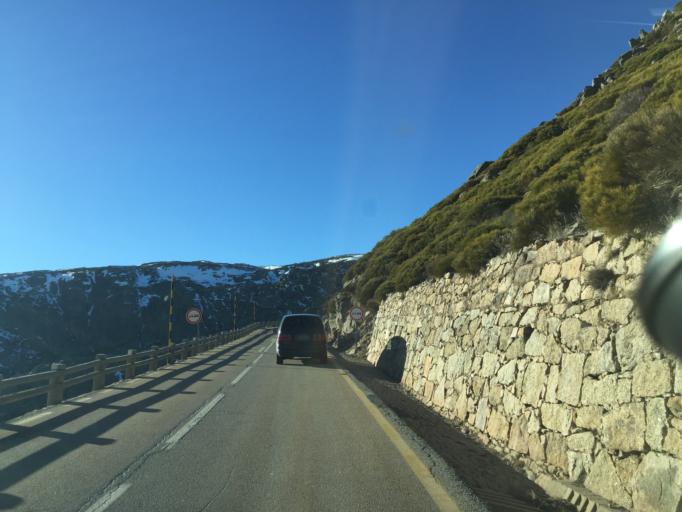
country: PT
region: Castelo Branco
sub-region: Covilha
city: Covilha
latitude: 40.3200
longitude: -7.5985
